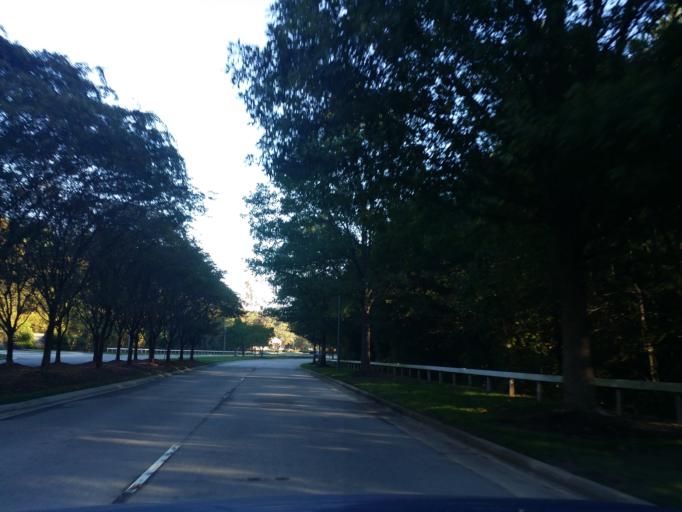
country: US
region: North Carolina
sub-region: Wake County
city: Morrisville
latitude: 35.8239
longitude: -78.8068
